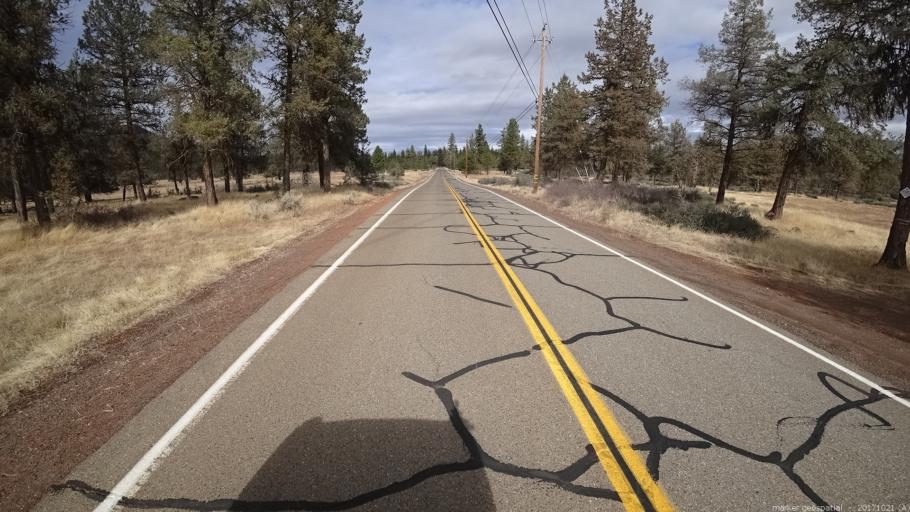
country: US
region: California
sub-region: Shasta County
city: Burney
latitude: 40.9228
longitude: -121.6466
